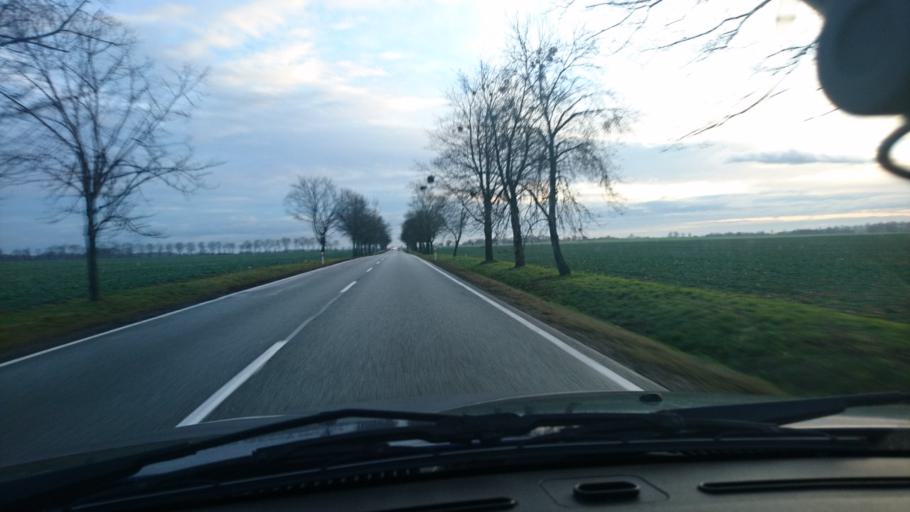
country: PL
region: Opole Voivodeship
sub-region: Powiat kluczborski
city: Byczyna
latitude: 51.0764
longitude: 18.2012
